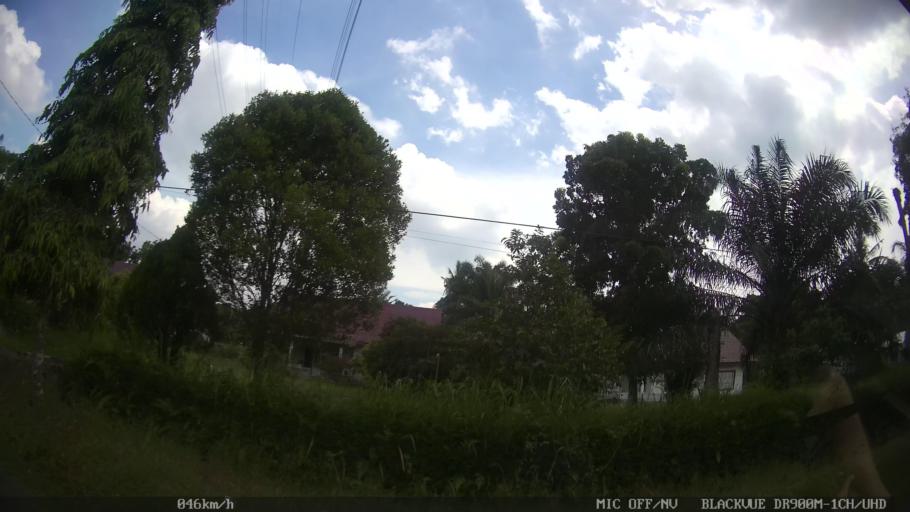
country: ID
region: North Sumatra
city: Binjai
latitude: 3.6354
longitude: 98.5135
